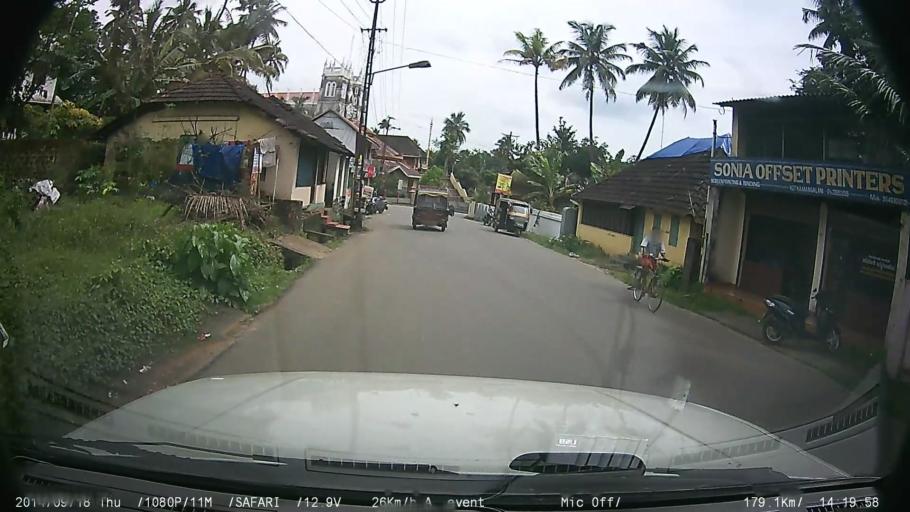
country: IN
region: Kerala
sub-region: Ernakulam
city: Kotamangalam
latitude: 10.0660
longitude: 76.6277
